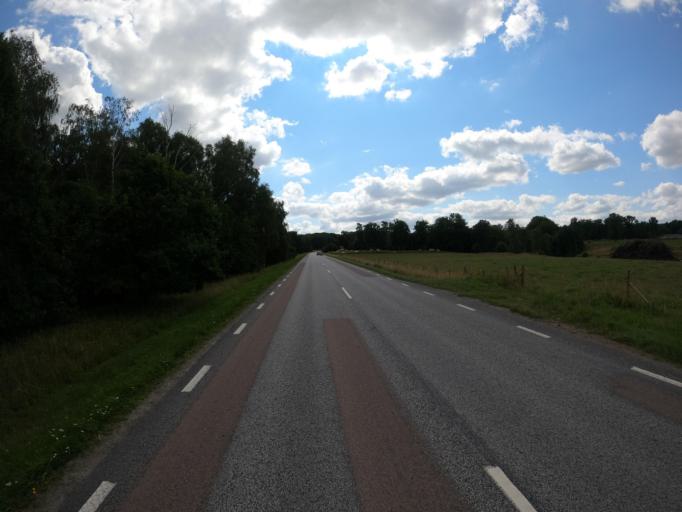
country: SE
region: Skane
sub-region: Lunds Kommun
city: Veberod
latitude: 55.6207
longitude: 13.4929
